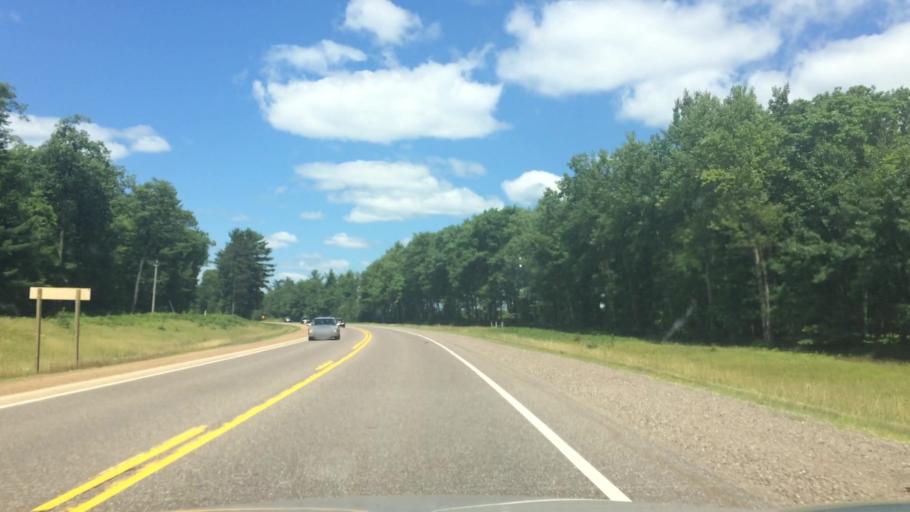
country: US
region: Wisconsin
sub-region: Vilas County
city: Lac du Flambeau
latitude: 45.9413
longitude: -89.6965
